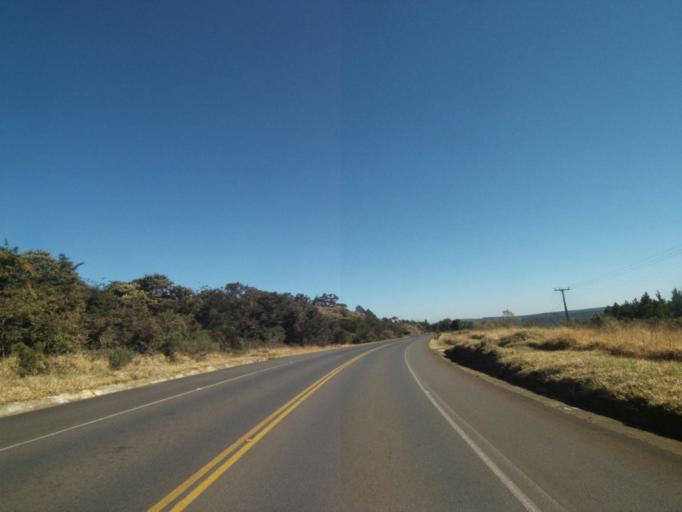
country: BR
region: Parana
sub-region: Tibagi
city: Tibagi
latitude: -24.4112
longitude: -50.3588
